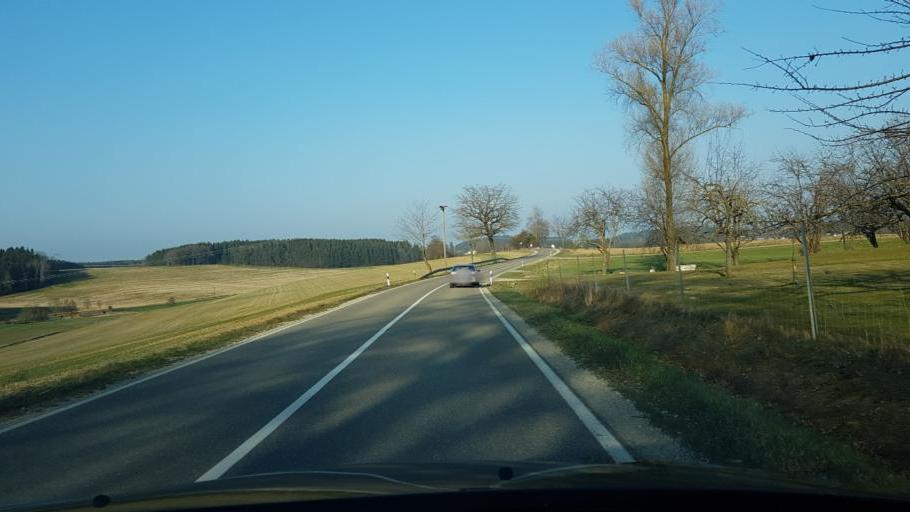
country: DE
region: Bavaria
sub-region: Upper Bavaria
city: Pfaffenhofen
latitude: 48.3712
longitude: 11.2007
